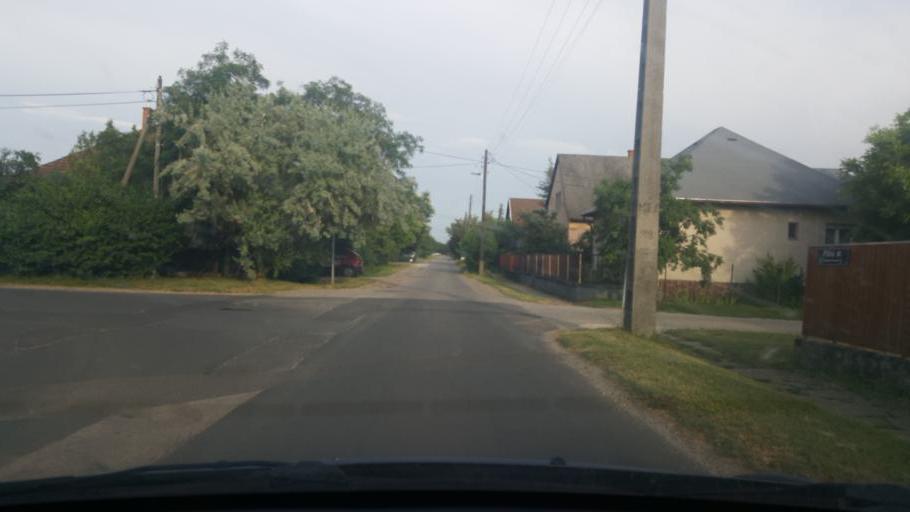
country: HU
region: Pest
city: Monor
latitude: 47.3386
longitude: 19.4476
